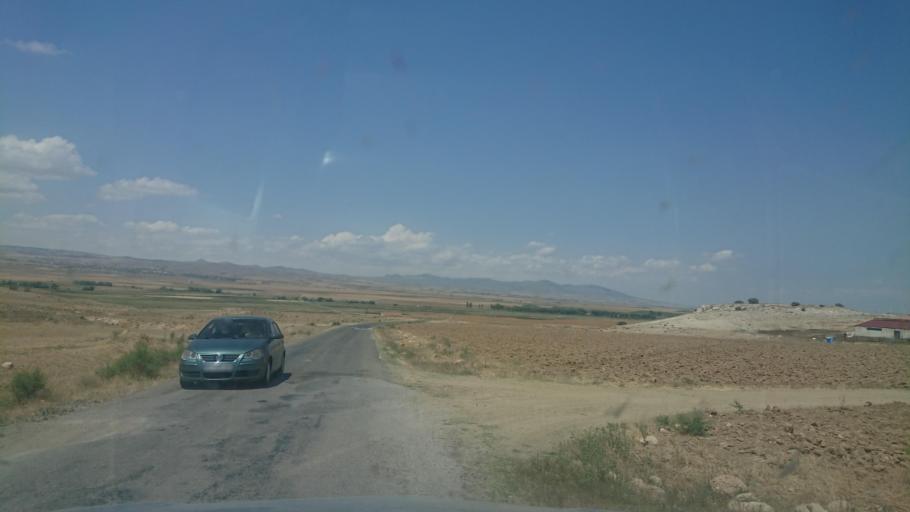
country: TR
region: Aksaray
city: Sariyahsi
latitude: 39.0056
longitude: 33.9167
